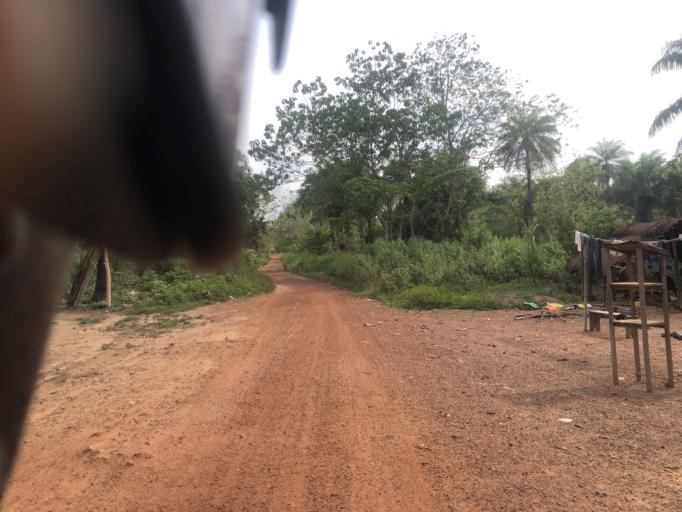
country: SL
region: Northern Province
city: Yonibana
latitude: 8.4405
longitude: -12.2436
